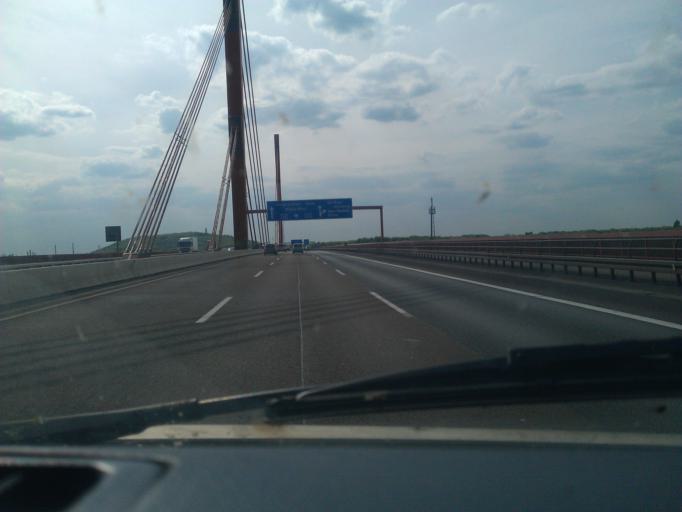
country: DE
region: North Rhine-Westphalia
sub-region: Regierungsbezirk Dusseldorf
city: Moers
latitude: 51.4809
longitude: 6.6845
